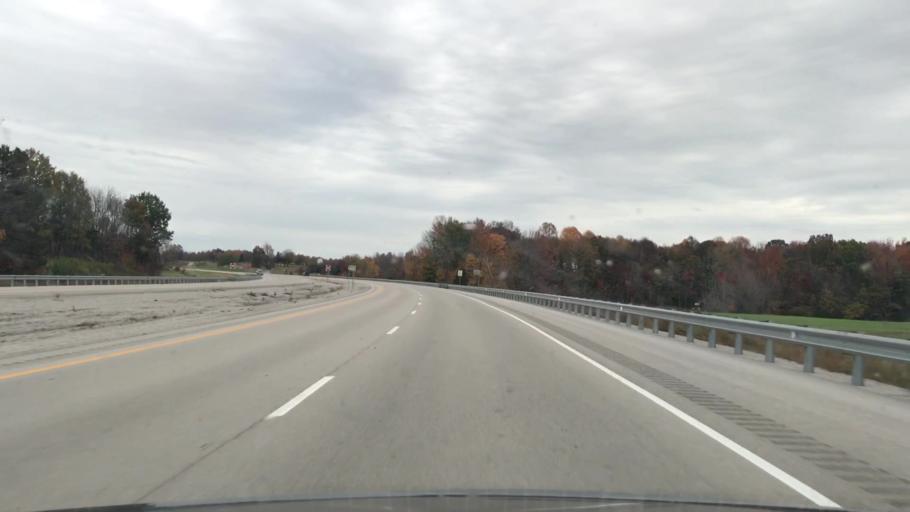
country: US
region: Kentucky
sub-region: Barren County
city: Glasgow
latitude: 36.9998
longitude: -85.9650
